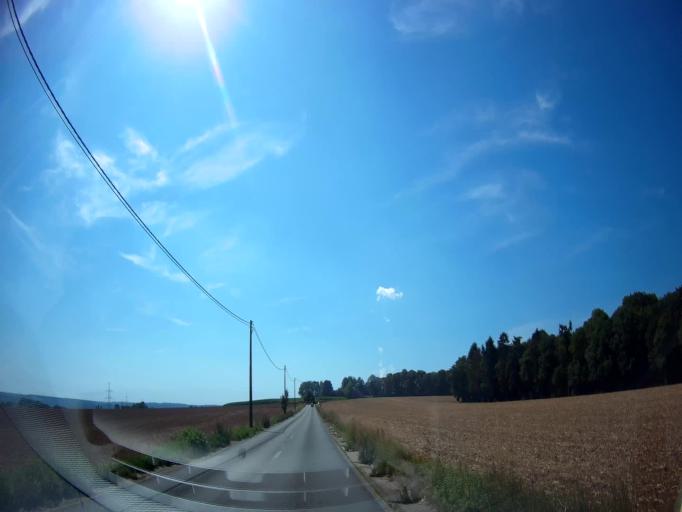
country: BE
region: Wallonia
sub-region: Province de Liege
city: Verlaine
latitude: 50.5761
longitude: 5.3292
